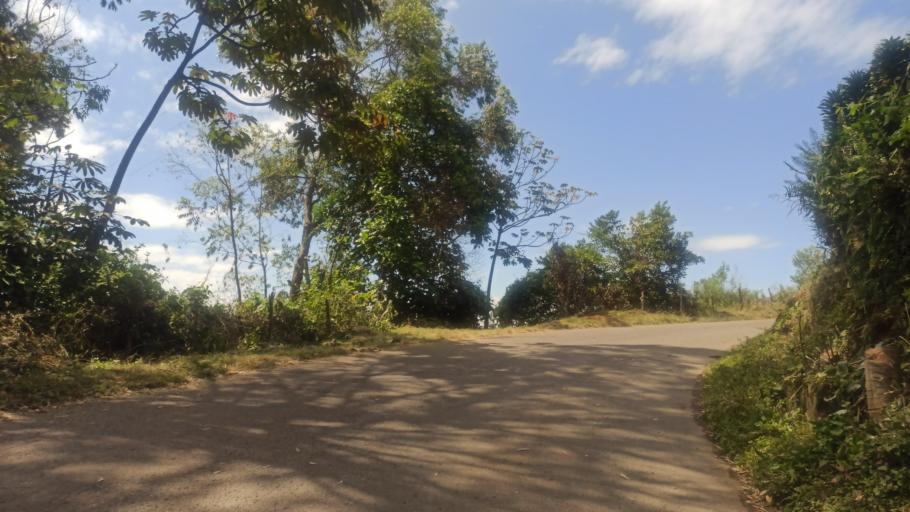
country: CO
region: Valle del Cauca
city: Jamundi
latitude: 3.1918
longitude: -76.6271
